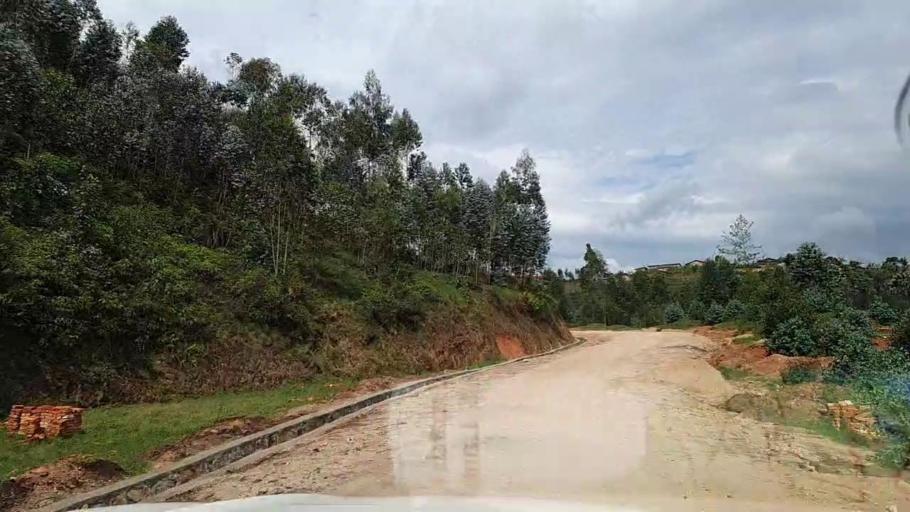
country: RW
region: Southern Province
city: Nzega
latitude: -2.3374
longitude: 29.4405
